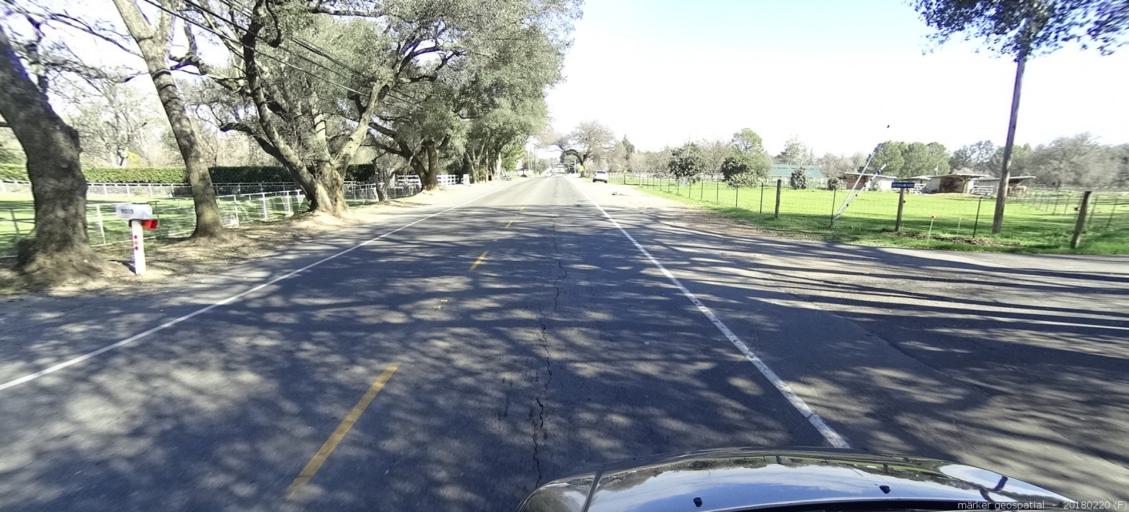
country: US
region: California
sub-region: Sacramento County
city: Orangevale
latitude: 38.7002
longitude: -121.2197
